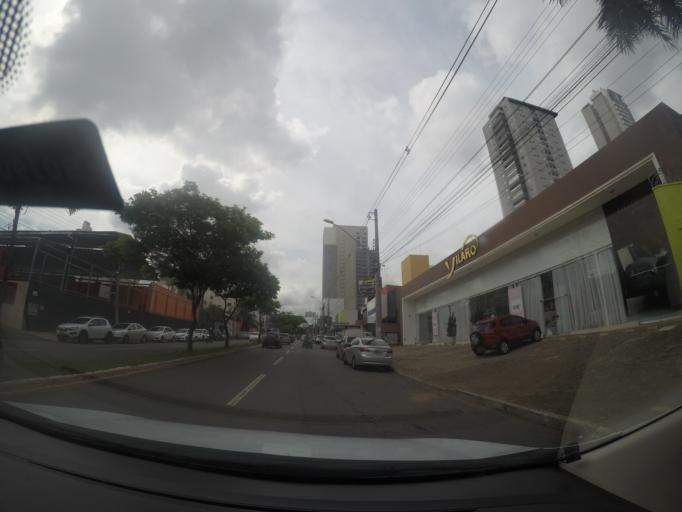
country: BR
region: Goias
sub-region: Goiania
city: Goiania
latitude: -16.7015
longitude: -49.2737
